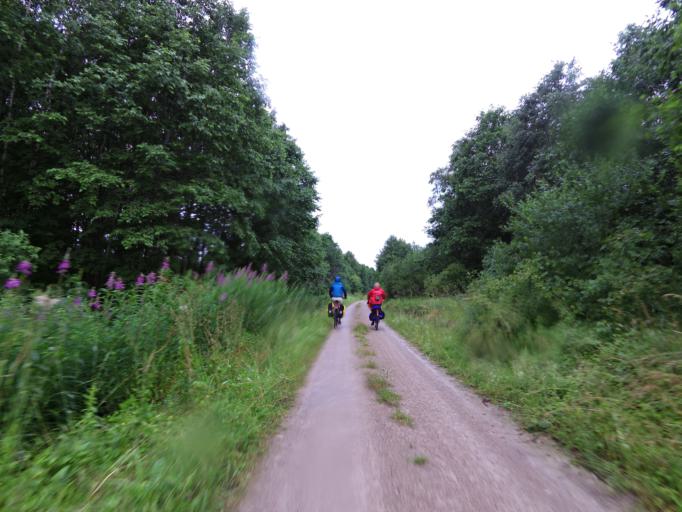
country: EE
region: Harju
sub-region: Nissi vald
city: Turba
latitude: 58.9884
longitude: 23.9802
